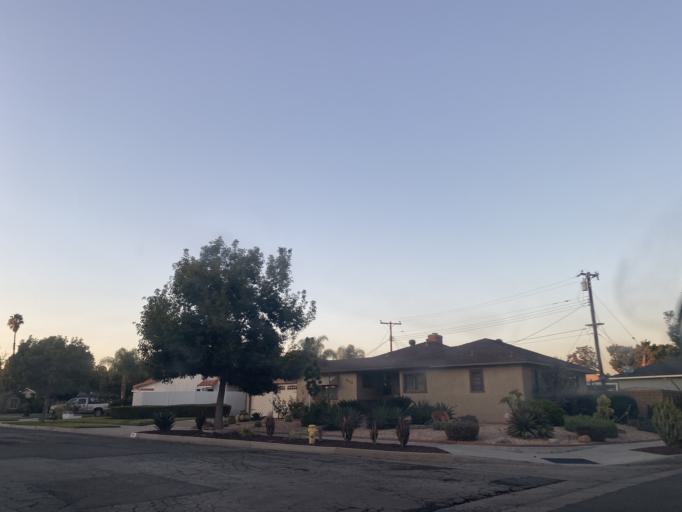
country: US
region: California
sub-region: Orange County
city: Fullerton
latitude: 33.8784
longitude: -117.9019
